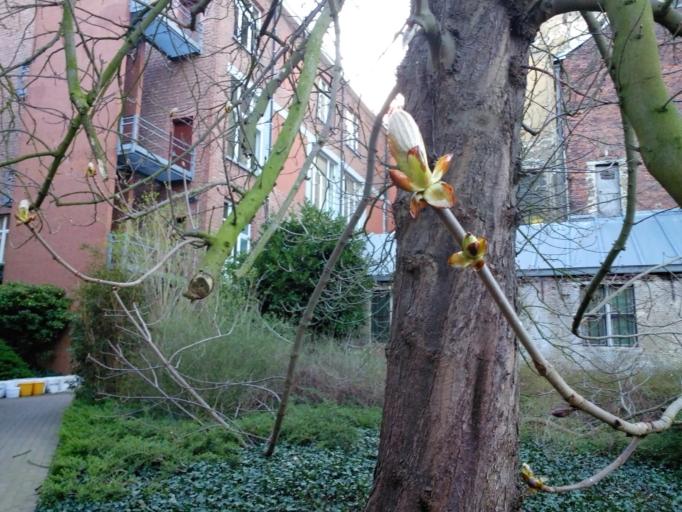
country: BE
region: Flanders
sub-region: Provincie Vlaams-Brabant
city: Leuven
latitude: 50.8763
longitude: 4.7017
